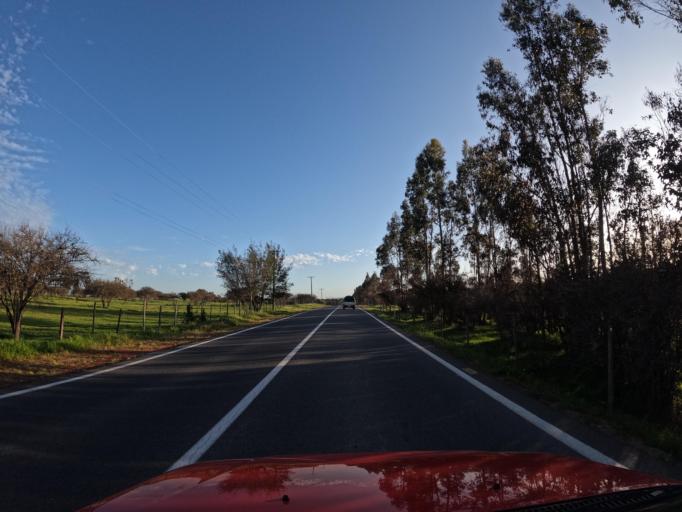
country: CL
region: O'Higgins
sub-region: Provincia de Colchagua
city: Santa Cruz
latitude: -34.2274
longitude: -71.7250
